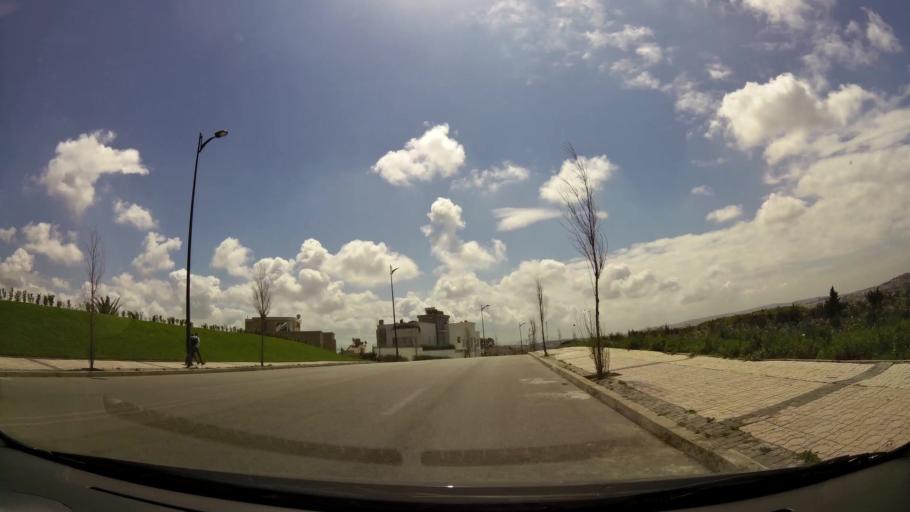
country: MA
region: Tanger-Tetouan
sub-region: Tanger-Assilah
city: Tangier
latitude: 35.7725
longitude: -5.8405
